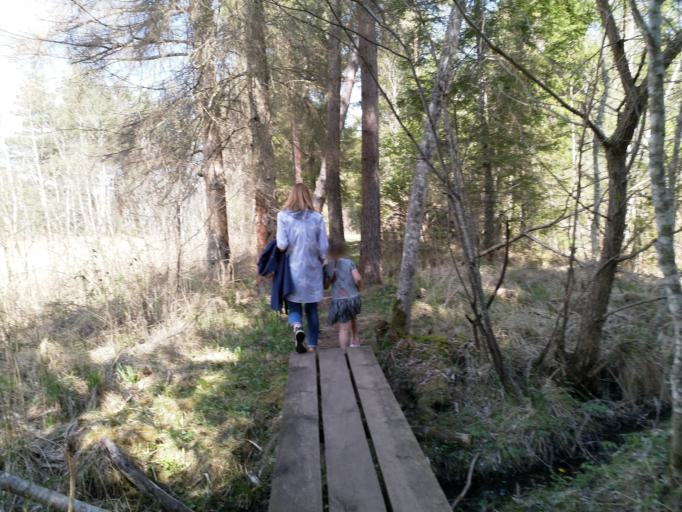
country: LV
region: Kandava
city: Kandava
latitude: 57.0222
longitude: 22.7748
